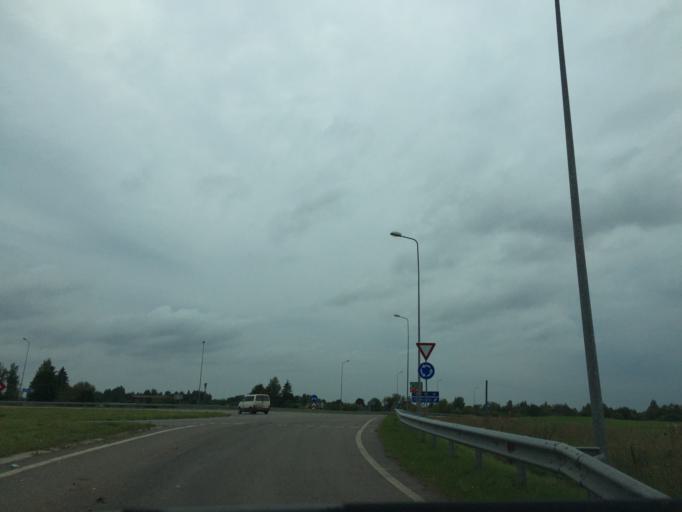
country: LV
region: Zilupes
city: Zilupe
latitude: 56.3832
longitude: 28.0805
